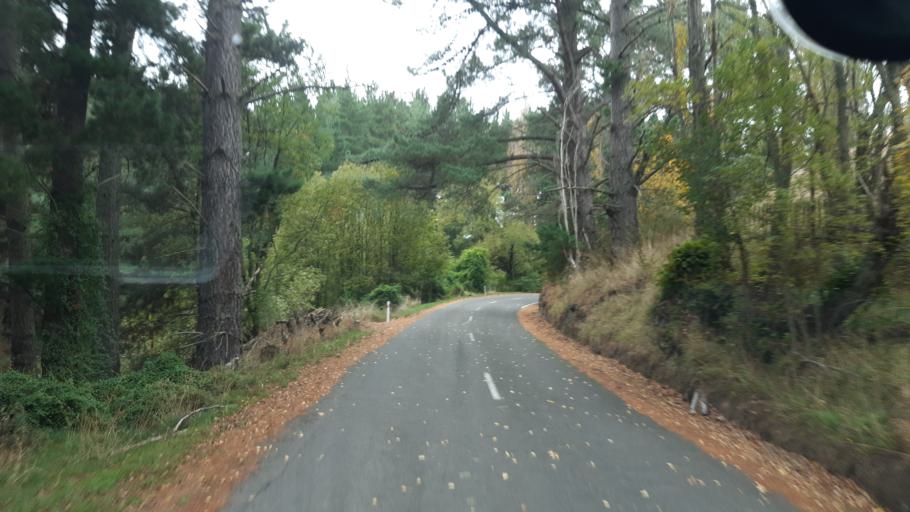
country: NZ
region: Manawatu-Wanganui
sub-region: Ruapehu District
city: Waiouru
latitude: -39.6133
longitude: 175.6164
